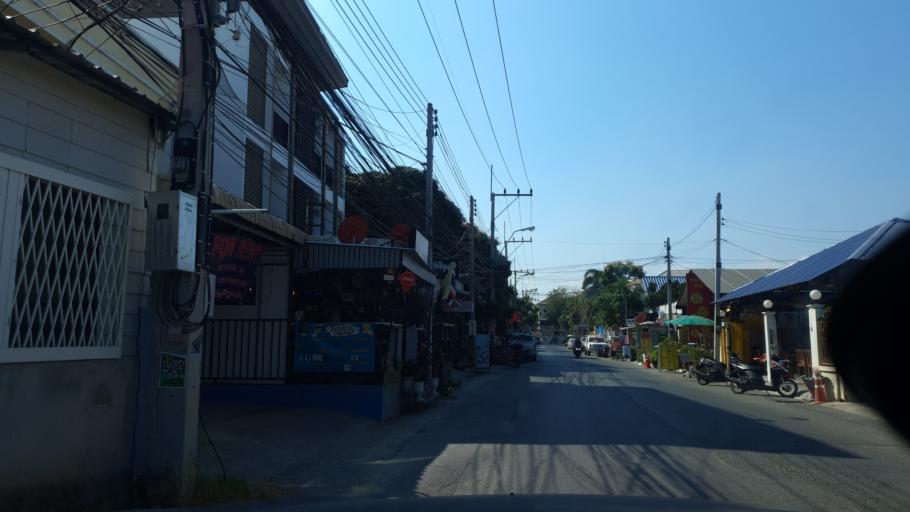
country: TH
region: Prachuap Khiri Khan
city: Hua Hin
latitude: 12.5546
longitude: 99.9544
